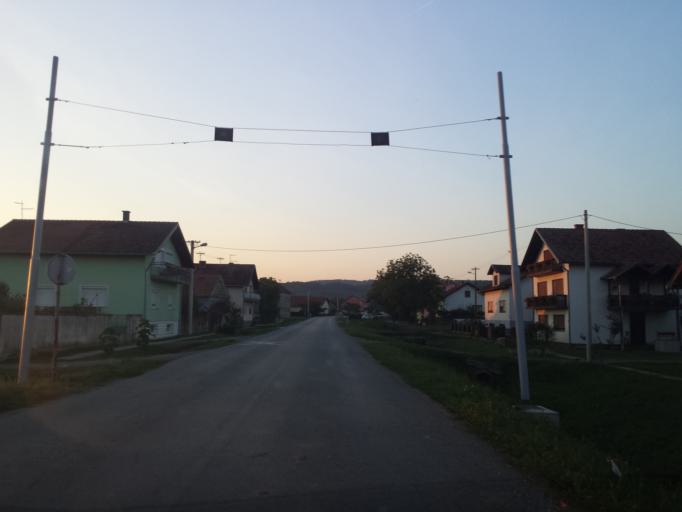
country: HR
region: Brodsko-Posavska
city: Oriovac
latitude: 45.1638
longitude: 17.8133
